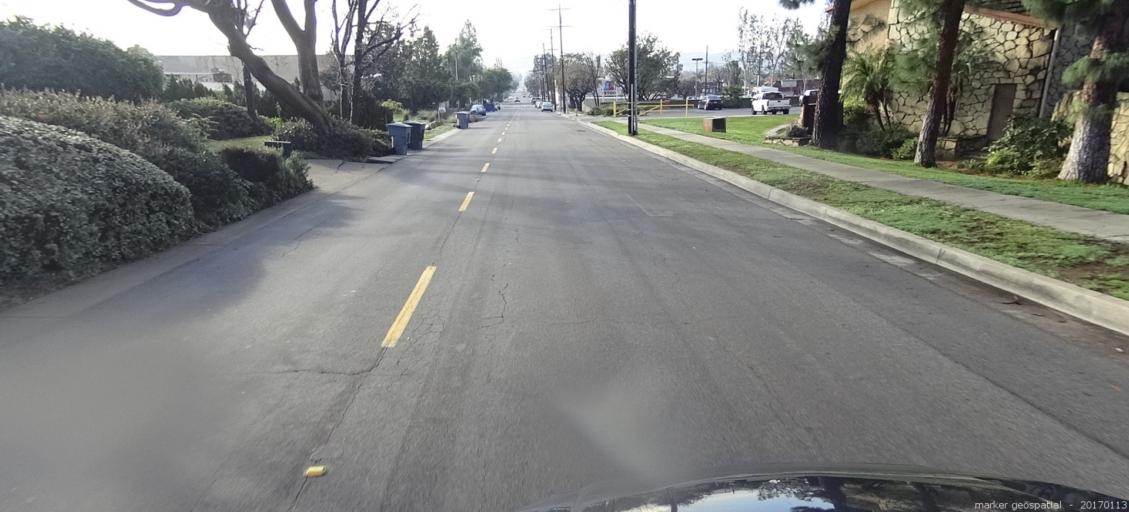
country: US
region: California
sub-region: Orange County
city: La Habra
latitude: 33.9413
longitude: -117.9592
